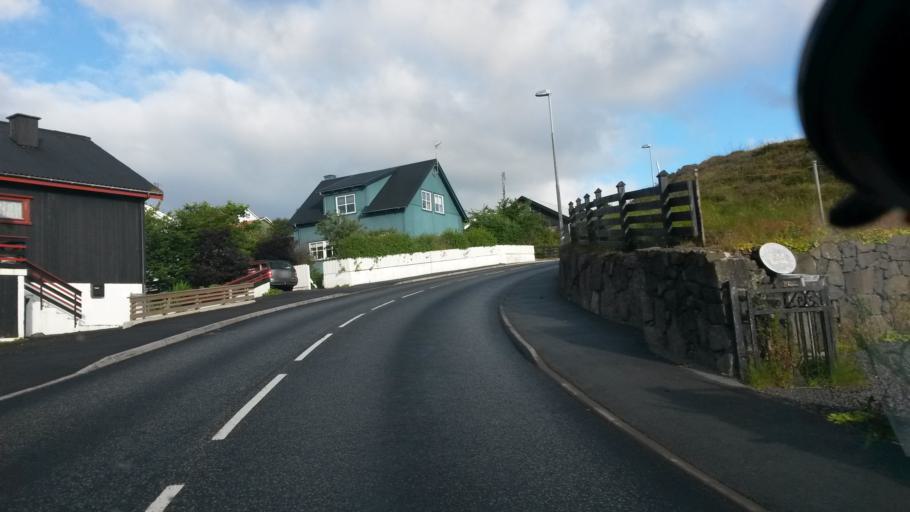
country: FO
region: Streymoy
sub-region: Torshavn
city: Torshavn
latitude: 62.0098
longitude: -6.7876
